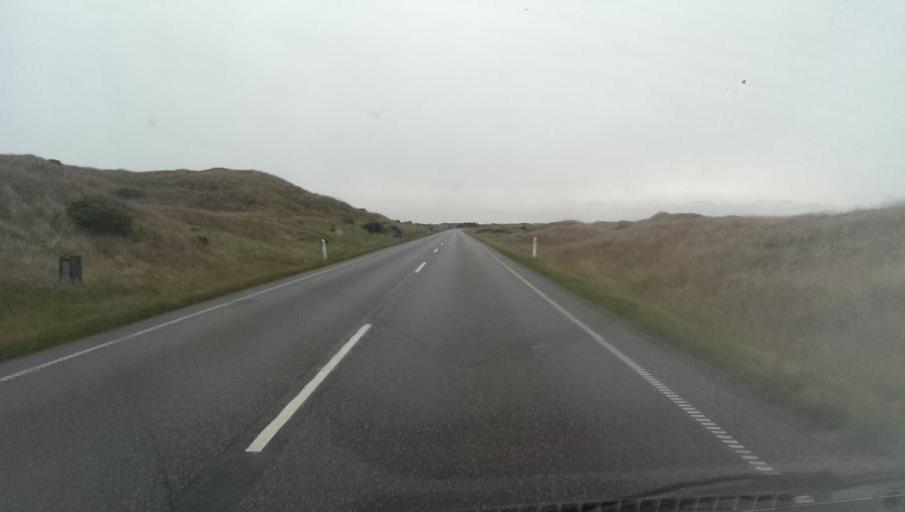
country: DK
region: Central Jutland
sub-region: Ringkobing-Skjern Kommune
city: Hvide Sande
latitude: 55.9174
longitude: 8.1637
